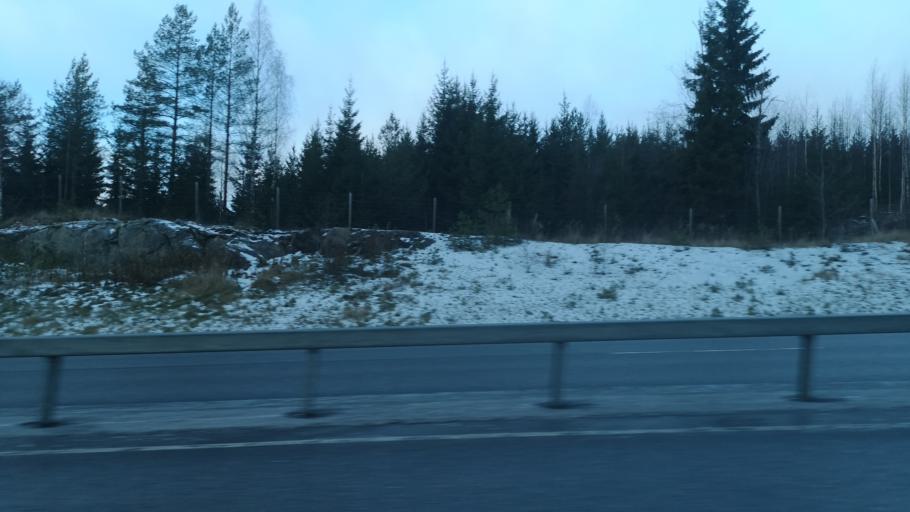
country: FI
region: Southern Savonia
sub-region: Mikkeli
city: Maentyharju
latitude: 61.5097
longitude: 26.8033
